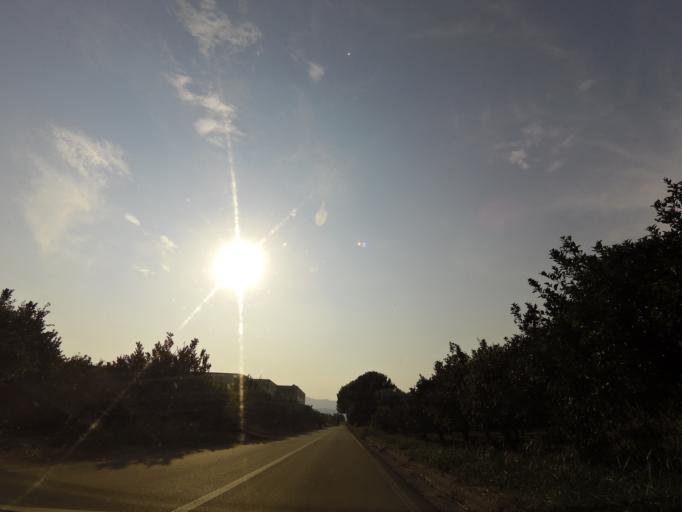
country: IT
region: Calabria
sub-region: Provincia di Reggio Calabria
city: Monasterace Marina
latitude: 38.4374
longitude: 16.5557
